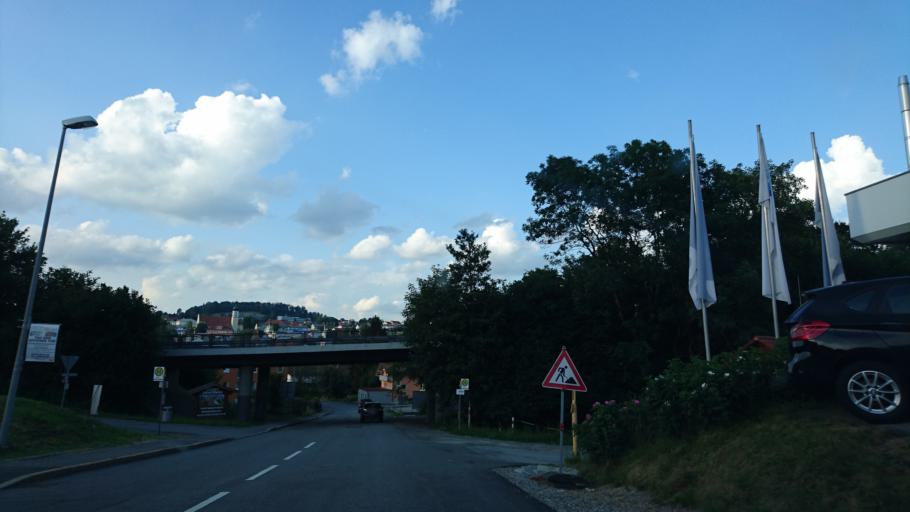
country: DE
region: Bavaria
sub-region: Lower Bavaria
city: Grafenau
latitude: 48.8517
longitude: 13.3940
